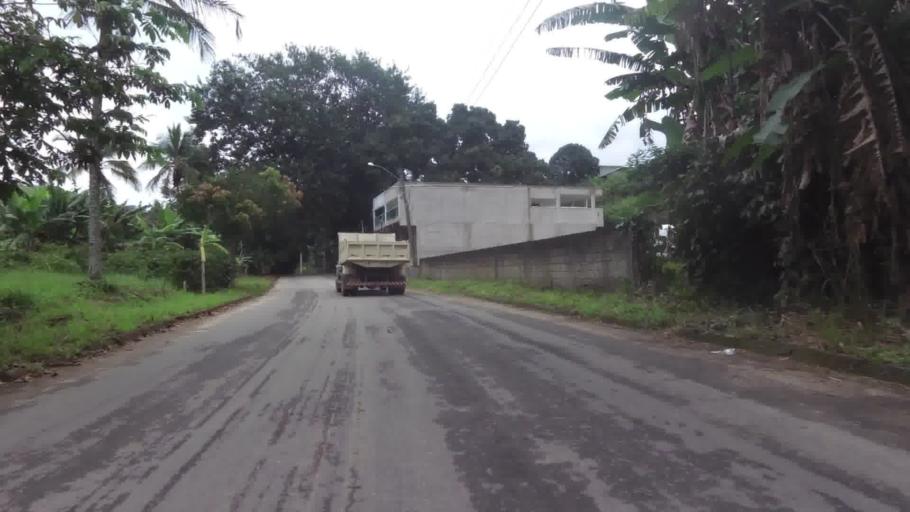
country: BR
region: Espirito Santo
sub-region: Iconha
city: Iconha
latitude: -20.7752
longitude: -40.8270
